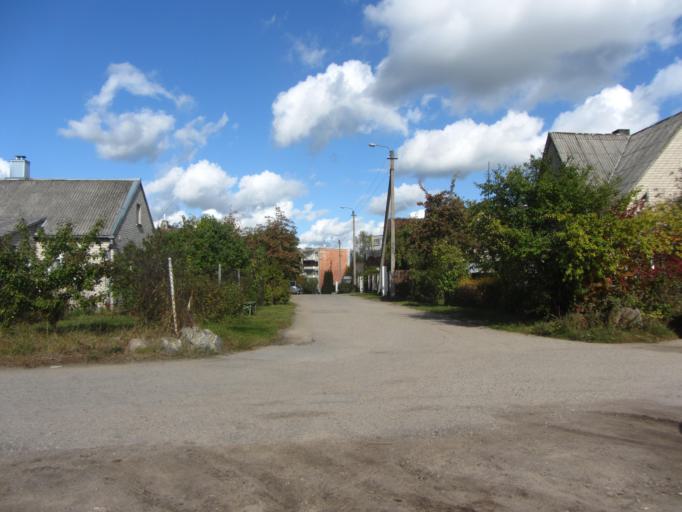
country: LT
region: Utenos apskritis
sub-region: Utena
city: Utena
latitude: 55.5053
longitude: 25.6146
